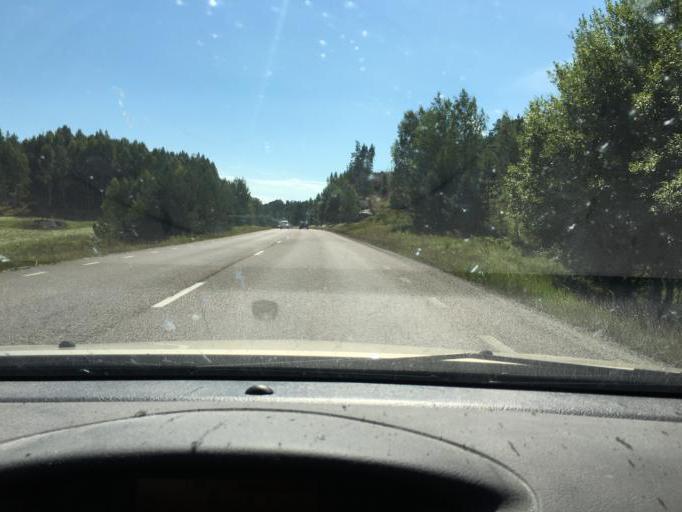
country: SE
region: Stockholm
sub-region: Varmdo Kommun
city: Gustavsberg
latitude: 59.2939
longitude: 18.3919
